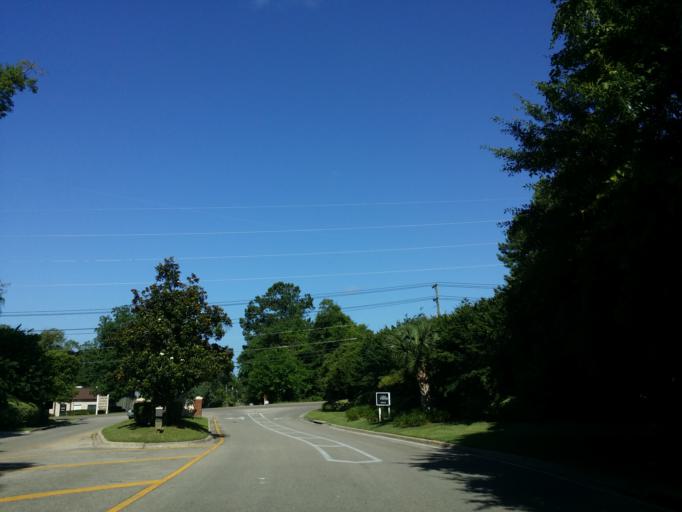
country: US
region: Florida
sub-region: Leon County
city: Tallahassee
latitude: 30.4578
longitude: -84.2216
